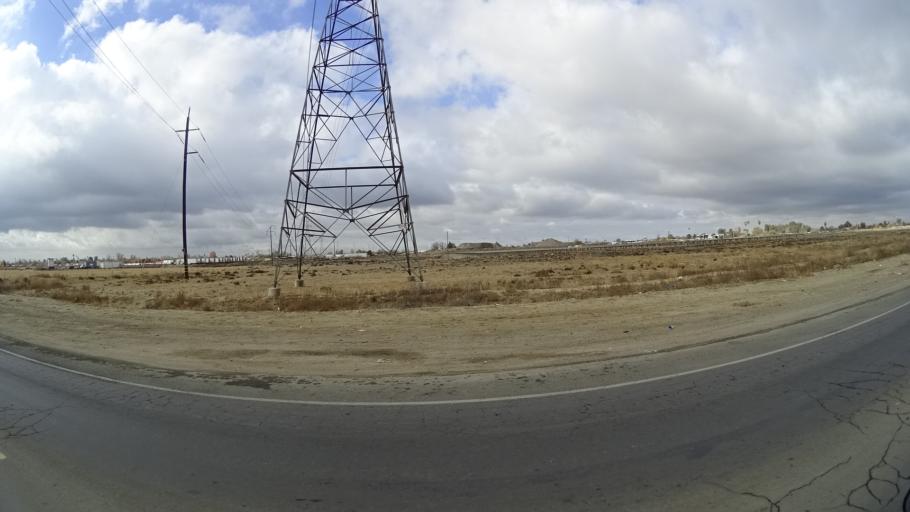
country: US
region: California
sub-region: Kern County
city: Greenfield
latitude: 35.3144
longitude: -118.9855
